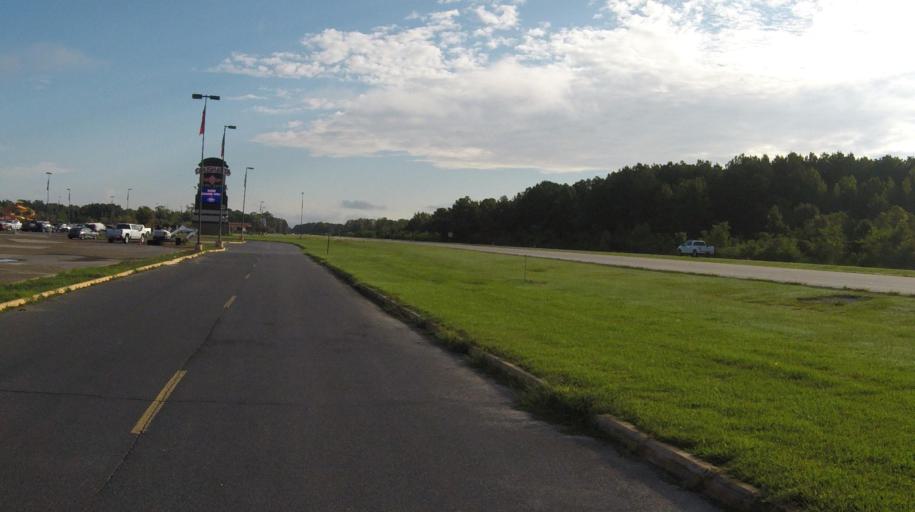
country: US
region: Louisiana
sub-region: Allen Parish
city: Kinder
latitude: 30.5430
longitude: -92.8131
